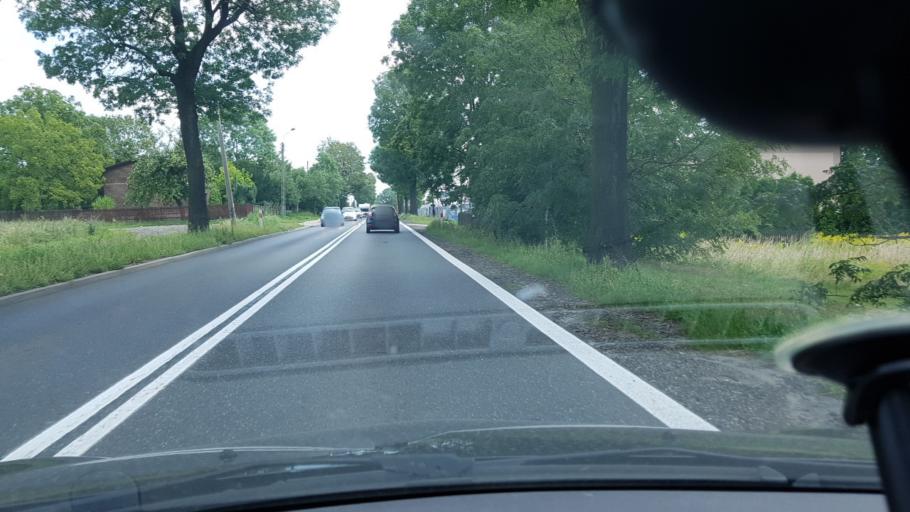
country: PL
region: Silesian Voivodeship
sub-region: Powiat bierunsko-ledzinski
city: Bojszowy
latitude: 50.0836
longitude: 19.1358
